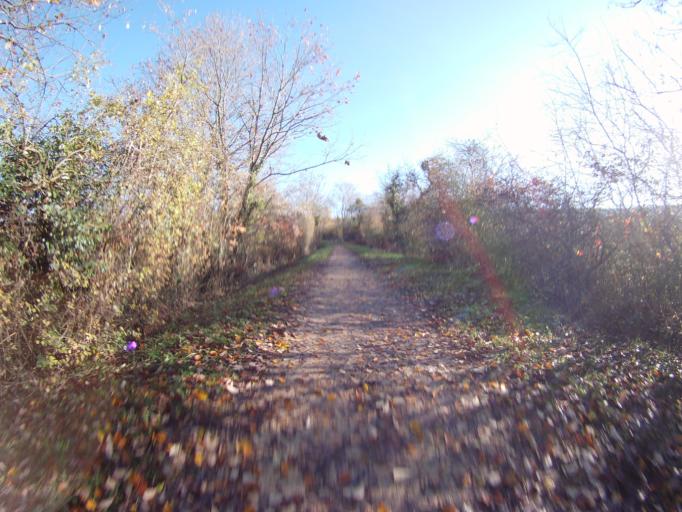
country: FR
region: Lorraine
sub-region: Departement de Meurthe-et-Moselle
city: Faulx
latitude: 48.7913
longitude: 6.2201
